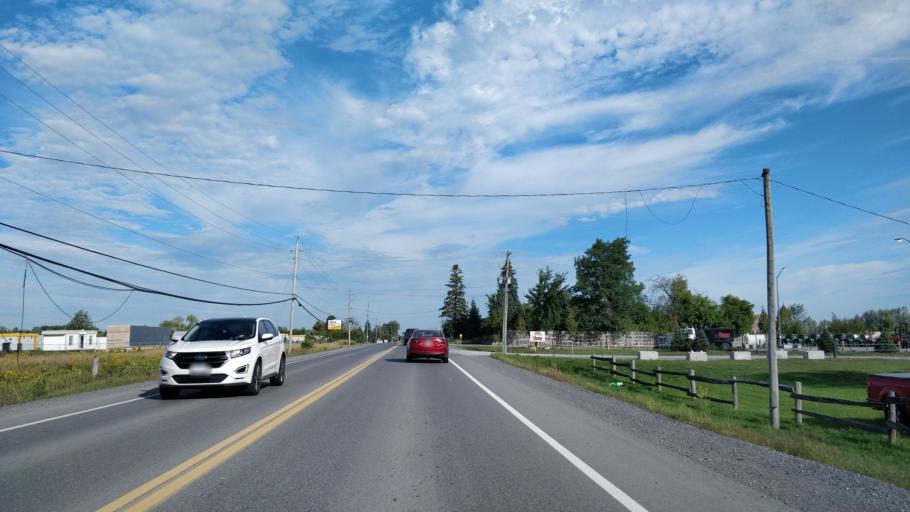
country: CA
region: Ontario
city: Bells Corners
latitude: 45.3003
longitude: -75.9808
